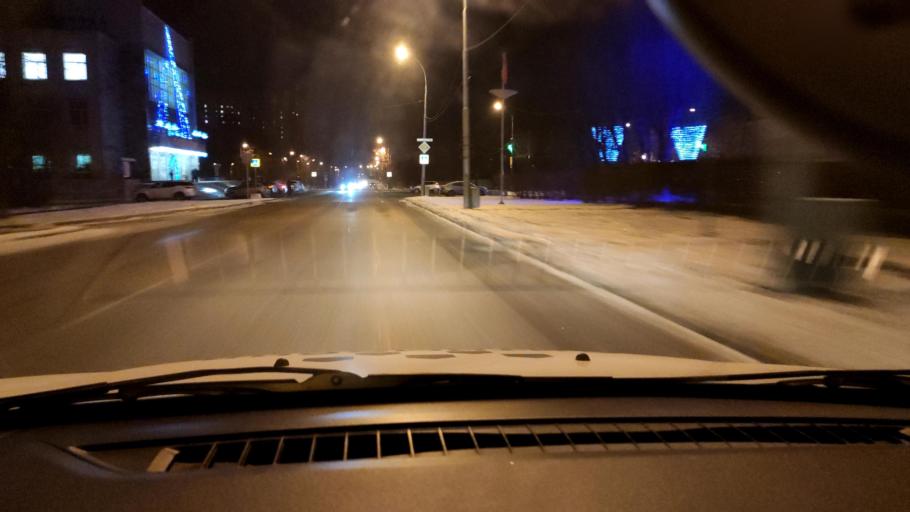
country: RU
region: Perm
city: Kultayevo
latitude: 57.9987
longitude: 55.9532
